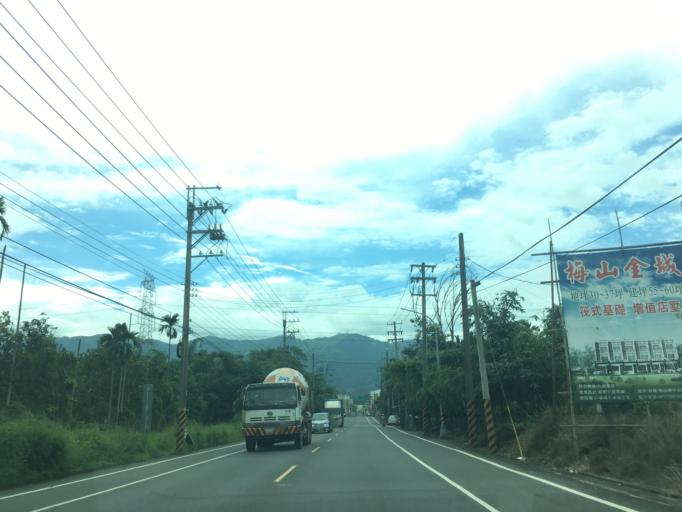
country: TW
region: Taiwan
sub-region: Yunlin
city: Douliu
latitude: 23.5888
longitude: 120.5470
